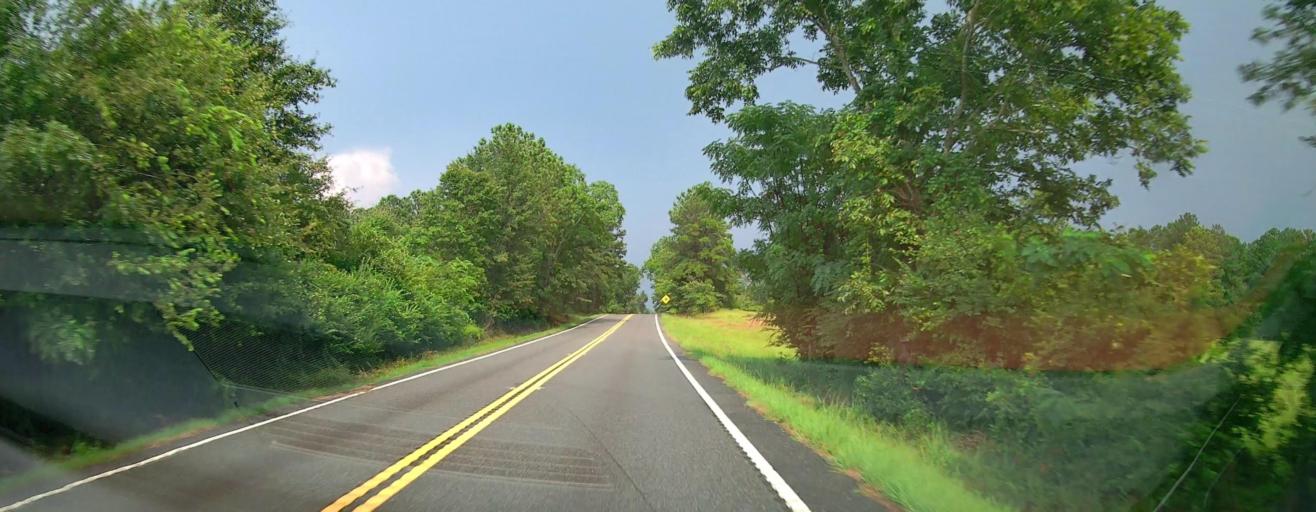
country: US
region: Georgia
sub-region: Twiggs County
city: Jeffersonville
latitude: 32.6058
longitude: -83.2836
